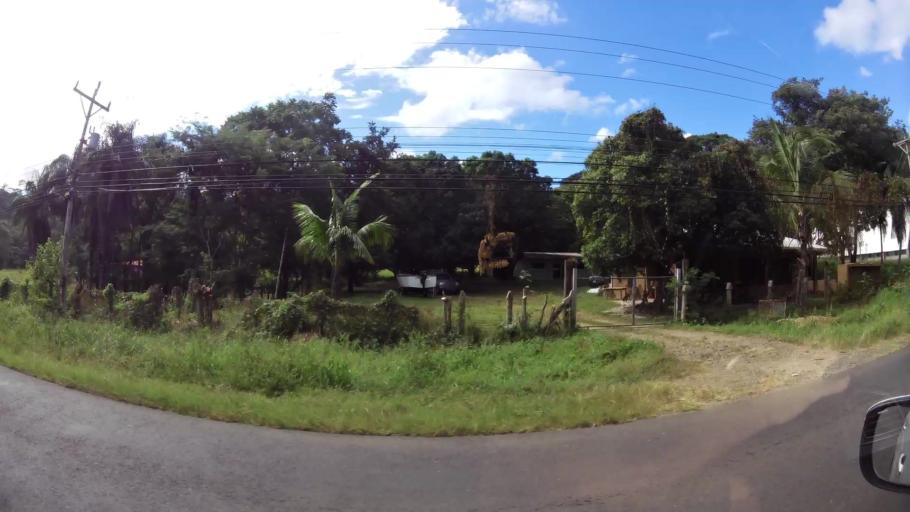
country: CR
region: Guanacaste
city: Santa Cruz
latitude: 10.3105
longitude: -85.8171
